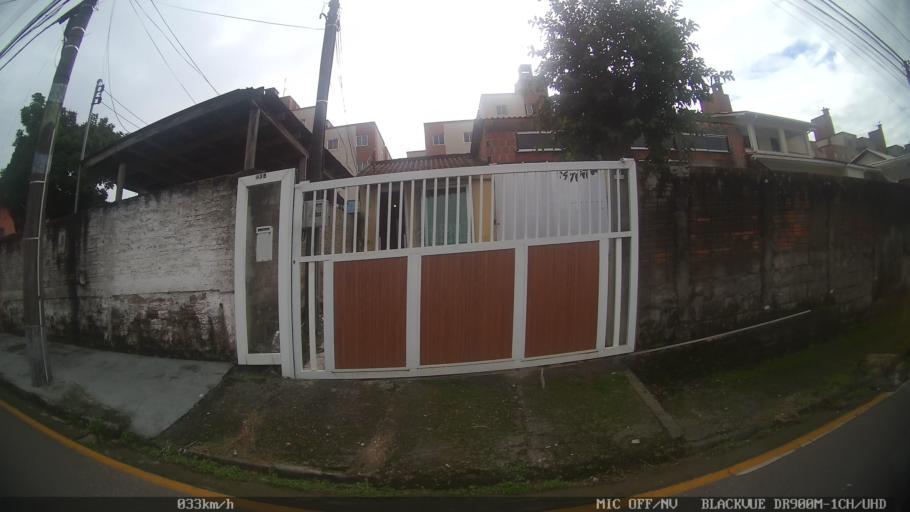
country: BR
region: Santa Catarina
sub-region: Sao Jose
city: Campinas
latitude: -27.5450
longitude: -48.6276
